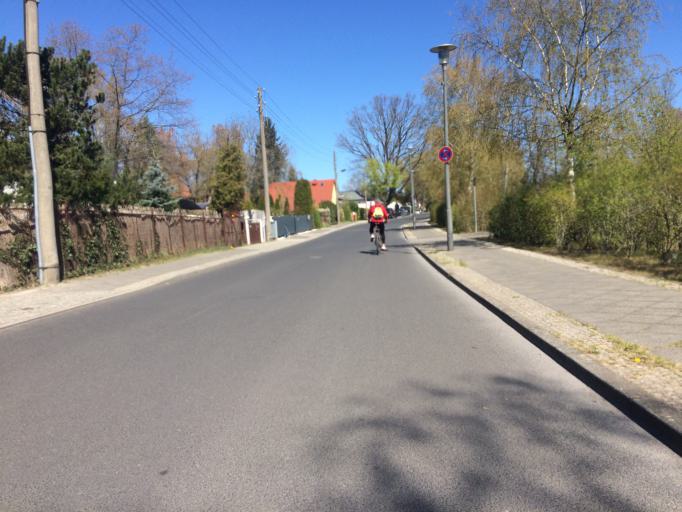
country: DE
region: Berlin
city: Rahnsdorf
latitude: 52.4308
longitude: 13.7131
